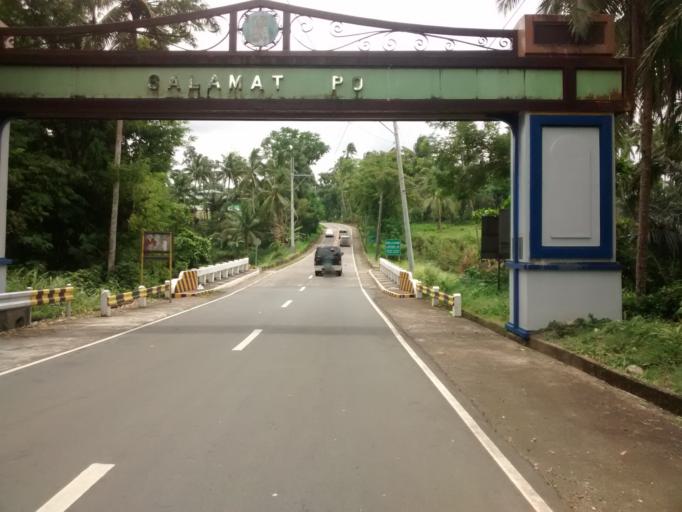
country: PH
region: Calabarzon
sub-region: Province of Laguna
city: Luisiana
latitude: 14.1564
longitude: 121.5353
